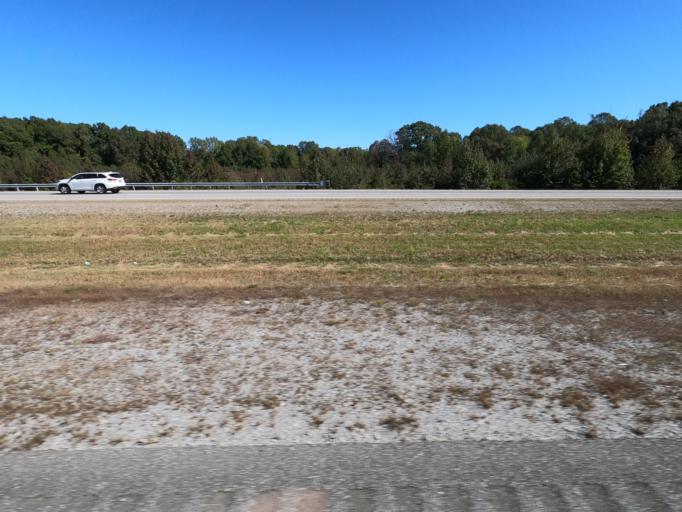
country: US
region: Tennessee
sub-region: Williamson County
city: Fairview
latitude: 35.9144
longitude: -87.1658
